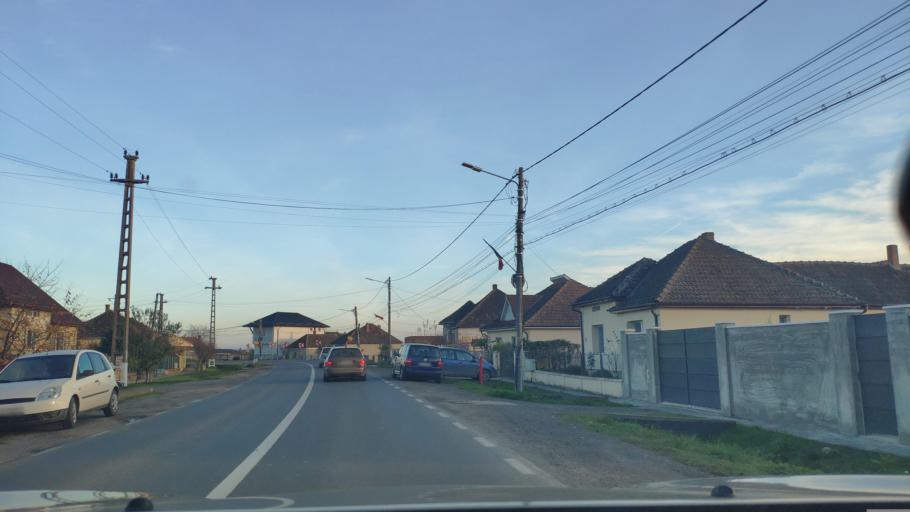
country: RO
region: Satu Mare
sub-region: Comuna Odoreu
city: Odoreu
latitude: 47.7925
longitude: 22.9977
